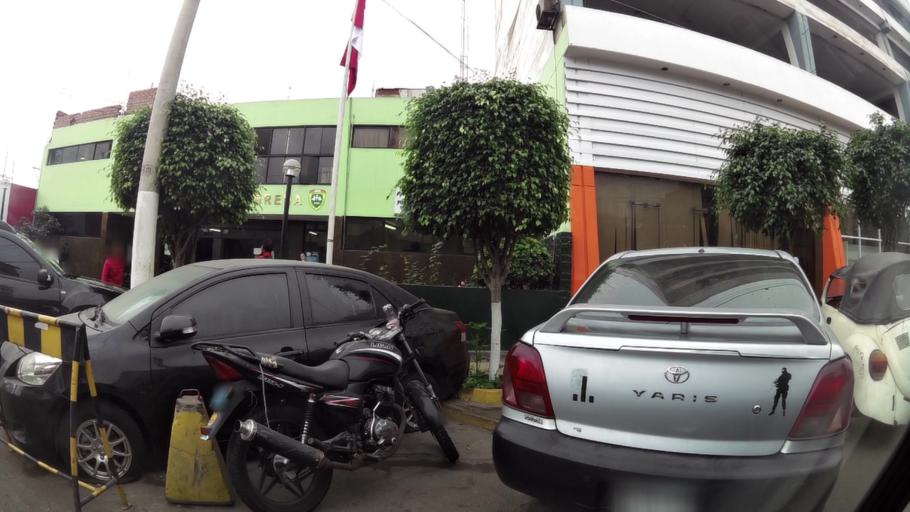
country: PE
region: Lima
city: Lima
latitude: -12.0672
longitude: -77.0528
